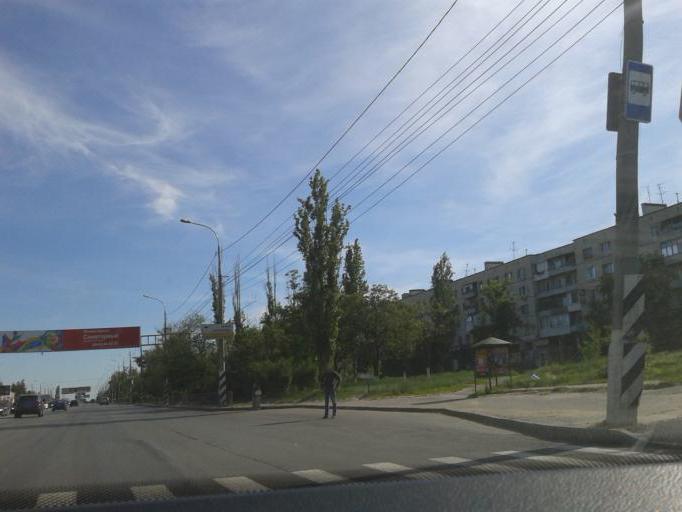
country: RU
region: Volgograd
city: Volgograd
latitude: 48.6525
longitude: 44.4358
